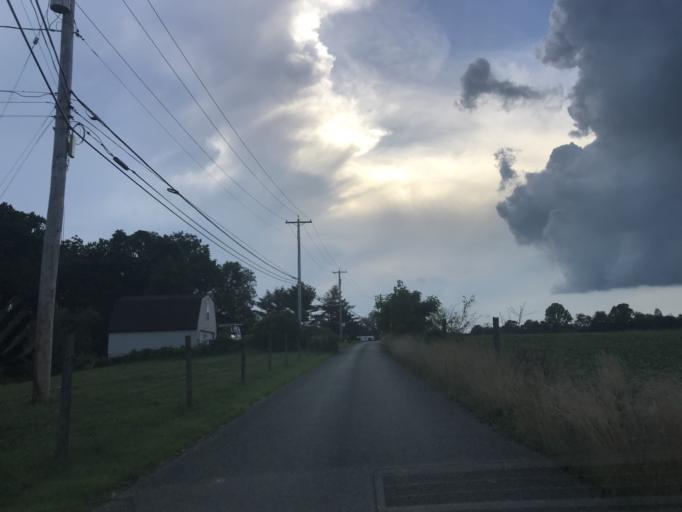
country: US
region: Maryland
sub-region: Harford County
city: Bel Air South
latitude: 39.5043
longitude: -76.2931
